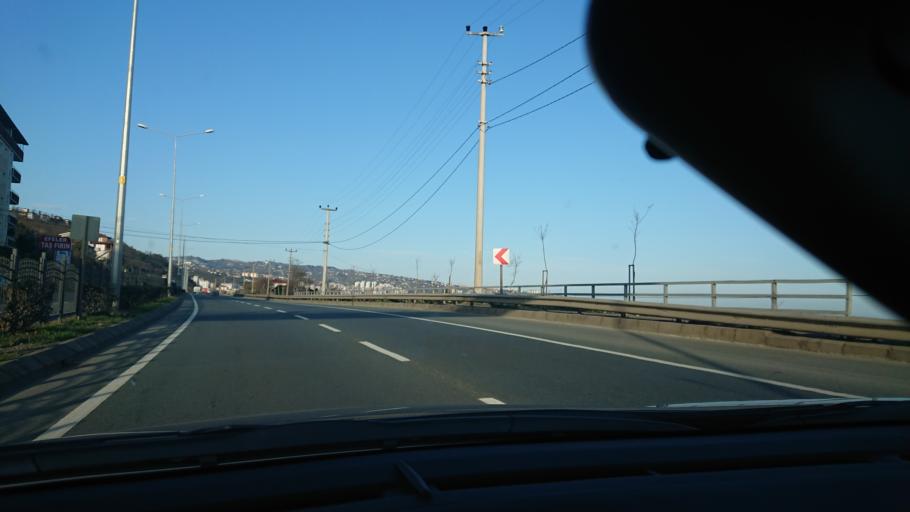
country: TR
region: Trabzon
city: Arsin
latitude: 40.9545
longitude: 39.8941
